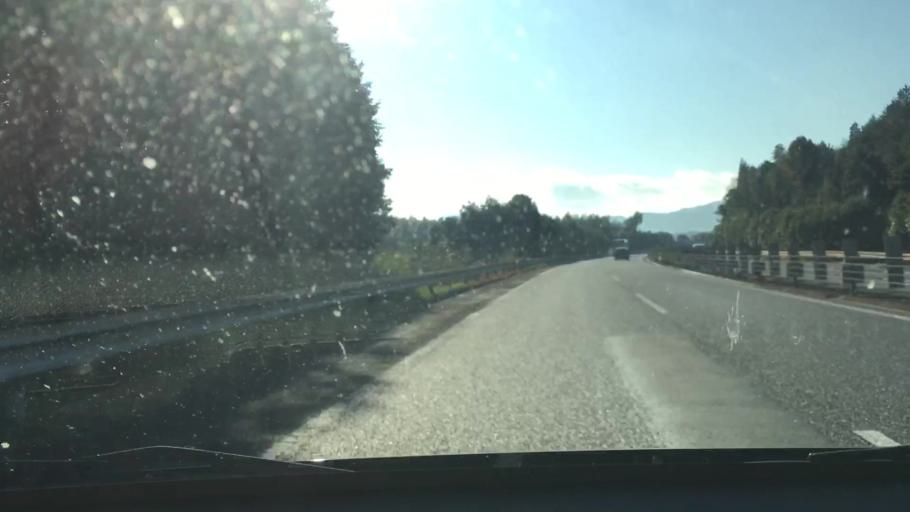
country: JP
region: Kagoshima
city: Okuchi-shinohara
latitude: 32.0175
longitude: 130.7693
